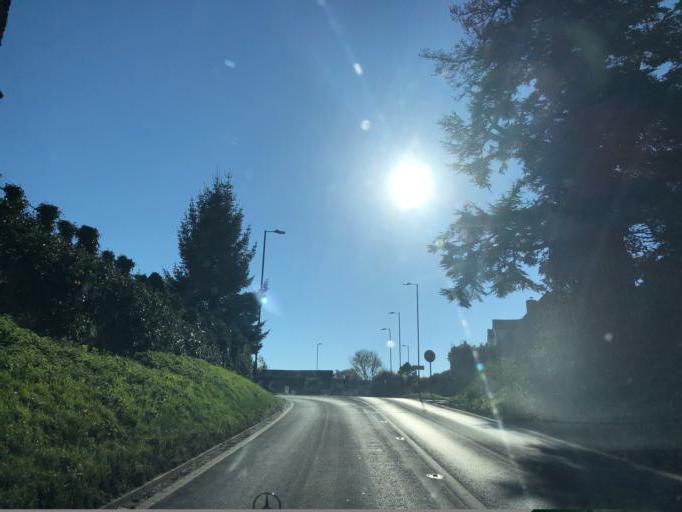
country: GB
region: England
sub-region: Warwickshire
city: Harbury
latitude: 52.2567
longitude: -1.4472
